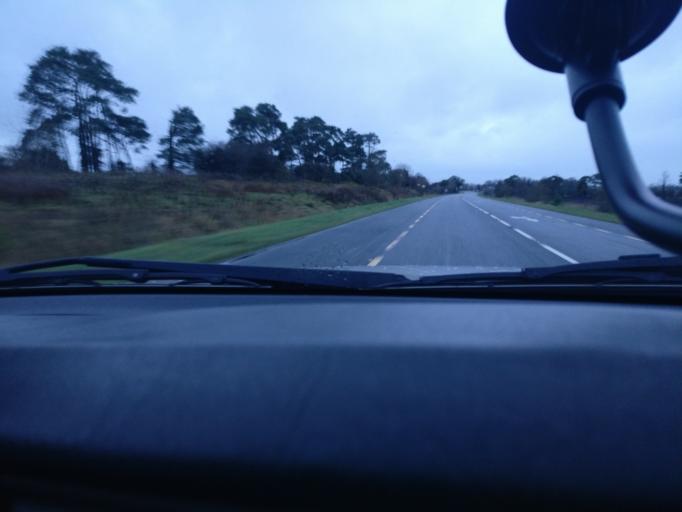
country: IE
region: Connaught
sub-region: County Galway
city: Ballinasloe
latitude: 53.2875
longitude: -8.3431
